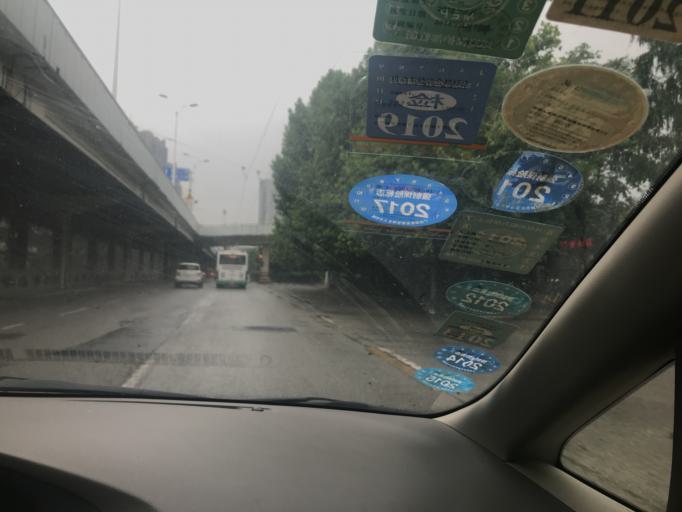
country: CN
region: Hubei
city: Jiang'an
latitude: 30.6168
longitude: 114.3055
